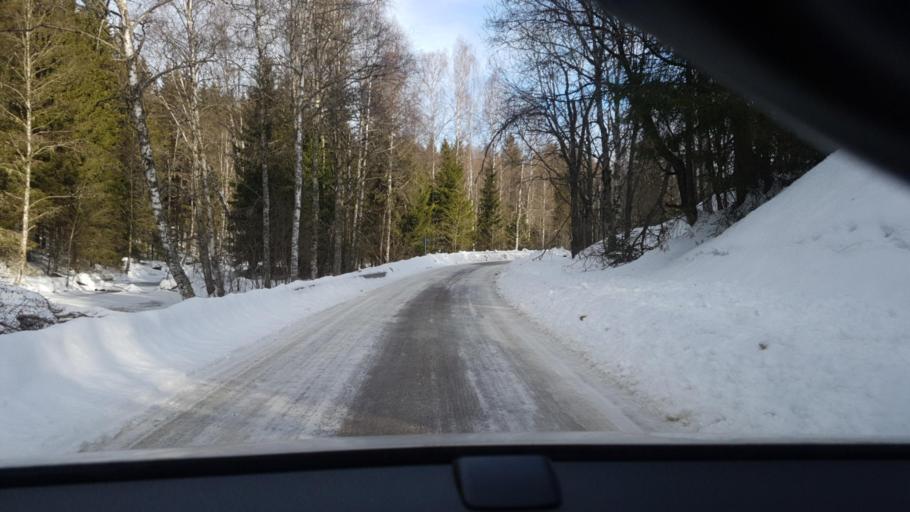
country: NO
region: Hedmark
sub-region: Eidskog
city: Skotterud
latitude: 59.8970
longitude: 11.9861
